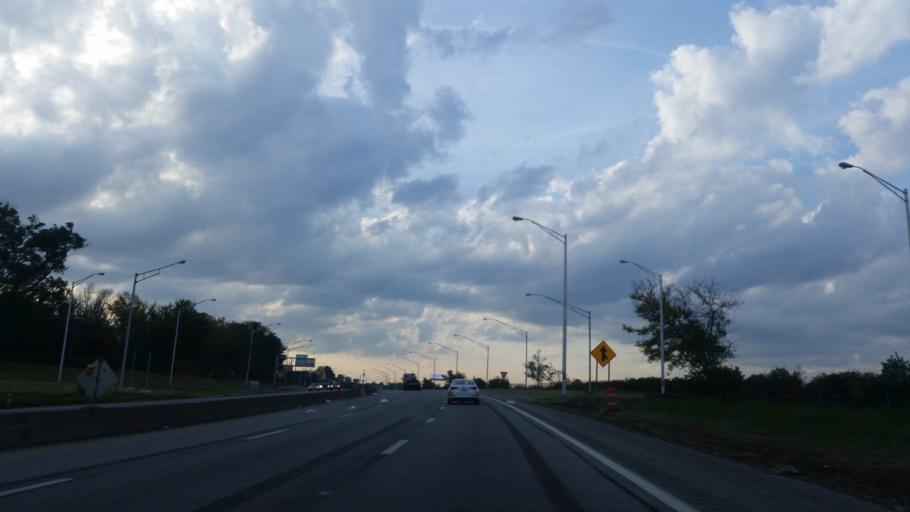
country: US
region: Ohio
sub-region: Cuyahoga County
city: Newburgh Heights
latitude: 41.4701
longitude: -81.6598
